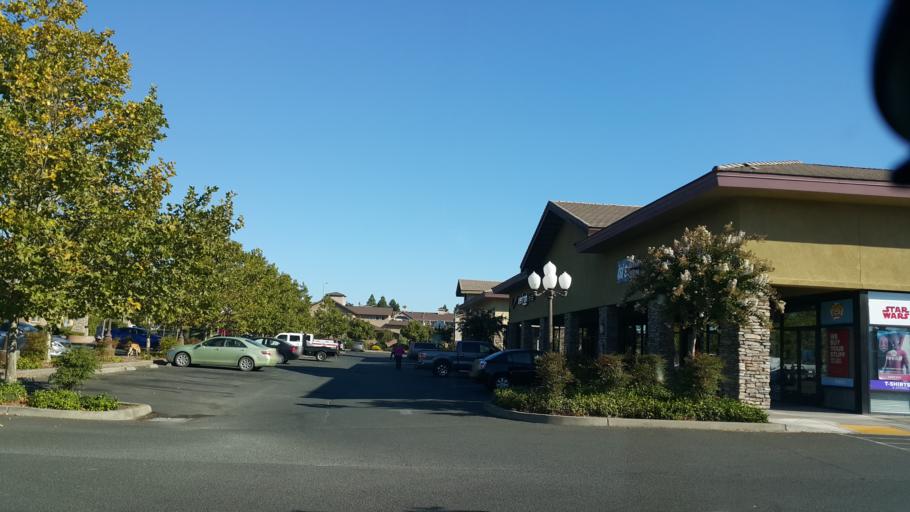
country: US
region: California
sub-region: Mendocino County
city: Ukiah
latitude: 39.1316
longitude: -123.1993
